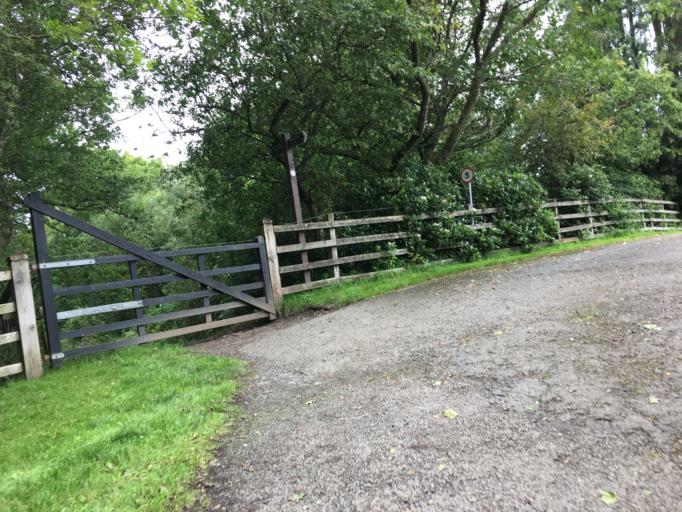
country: GB
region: Scotland
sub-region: Stirling
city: Killearn
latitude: 56.0325
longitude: -4.3878
